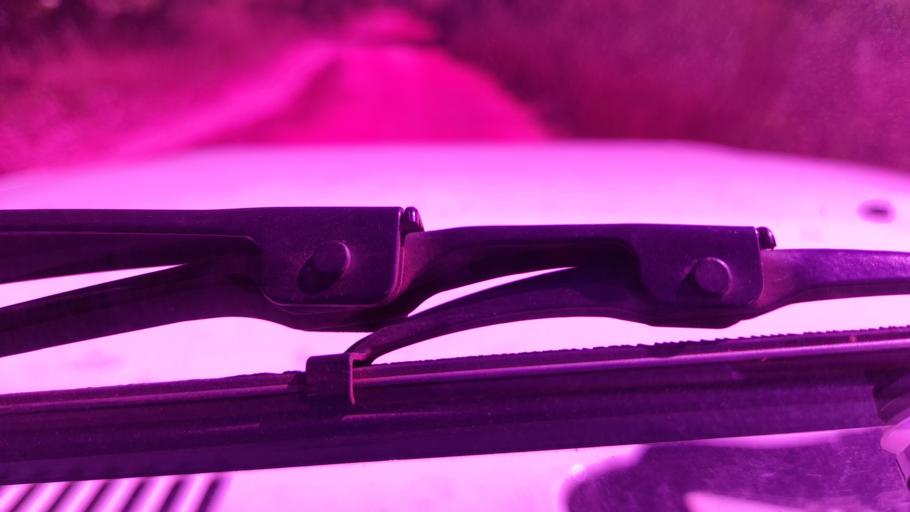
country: SN
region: Ziguinchor
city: Adeane
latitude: 12.4111
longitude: -15.7793
